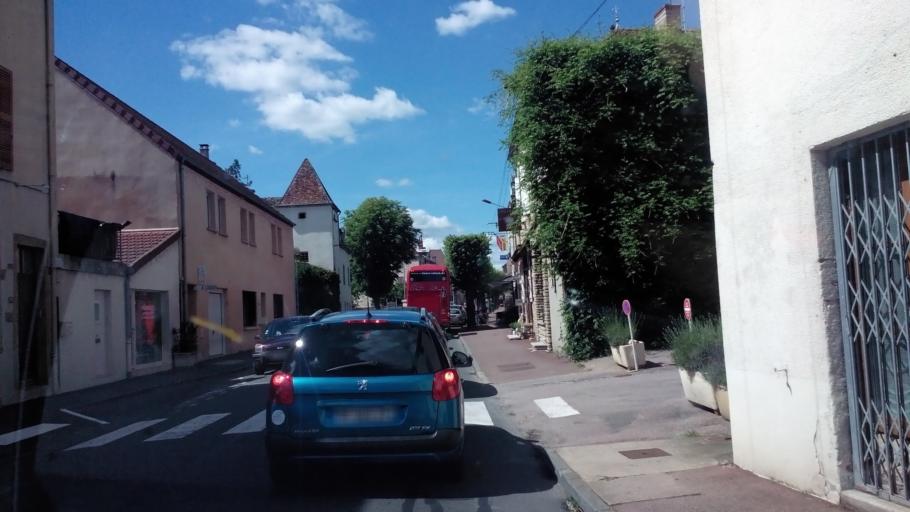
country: FR
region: Bourgogne
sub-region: Departement de Saone-et-Loire
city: Saint-Gengoux-le-National
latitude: 46.5446
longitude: 4.6865
